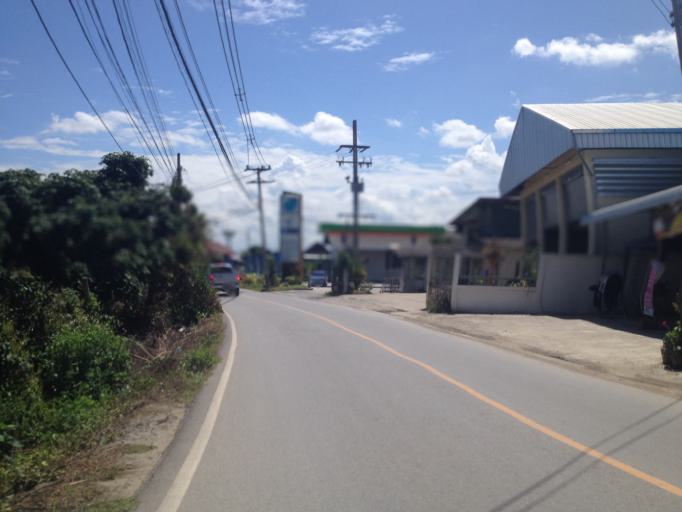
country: TH
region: Chiang Mai
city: Hang Dong
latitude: 18.6596
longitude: 98.9214
